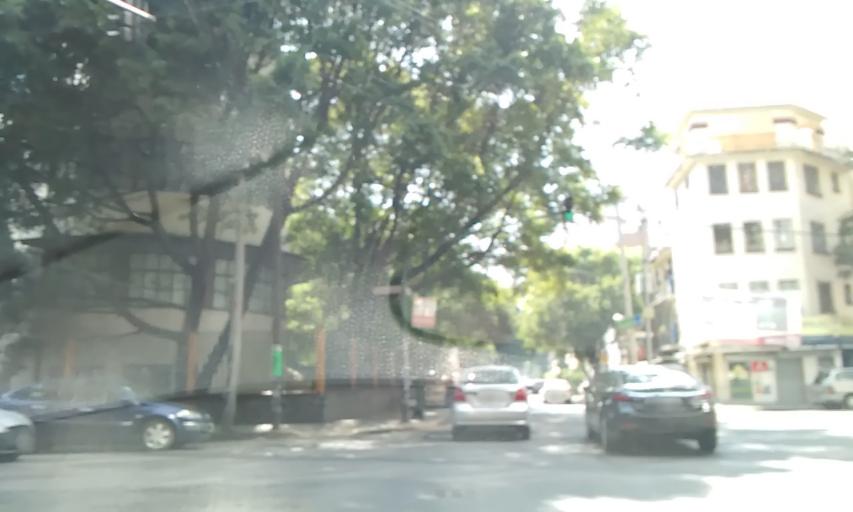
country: MX
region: Mexico City
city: Cuauhtemoc
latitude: 19.4337
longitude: -99.1663
